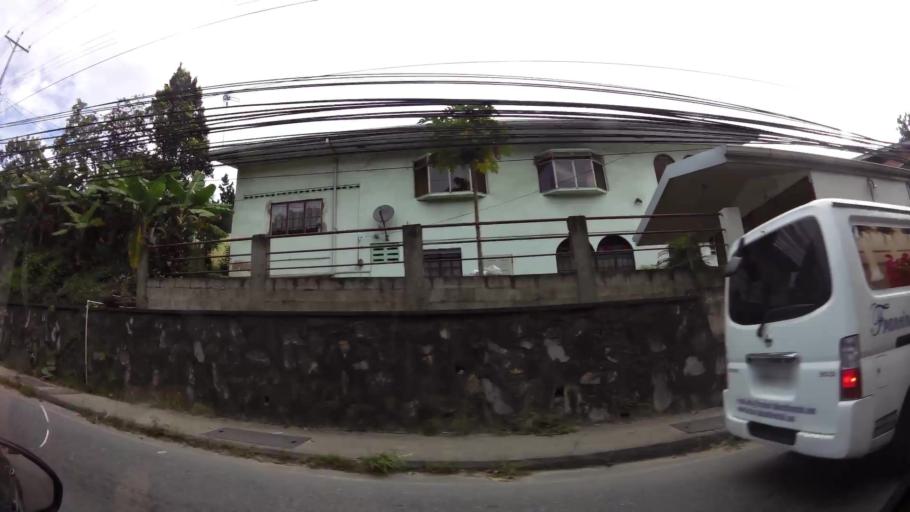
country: TT
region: San Juan/Laventille
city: Laventille
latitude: 10.6719
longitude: -61.4495
